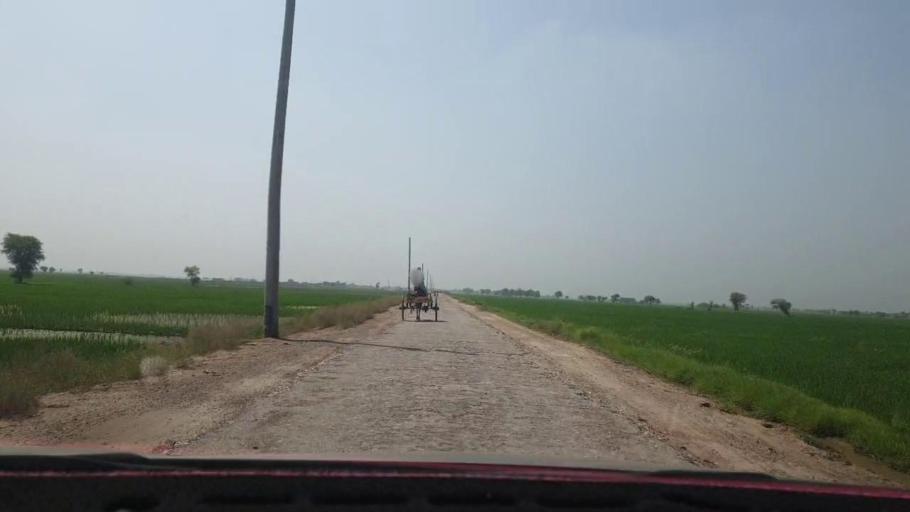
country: PK
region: Sindh
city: Warah
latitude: 27.4125
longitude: 67.8446
